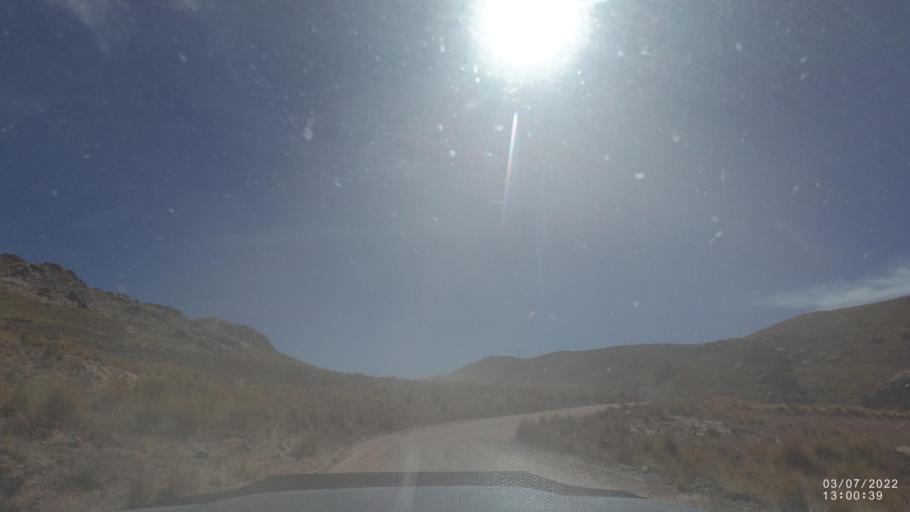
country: BO
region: Cochabamba
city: Colchani
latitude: -17.7130
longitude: -66.6899
